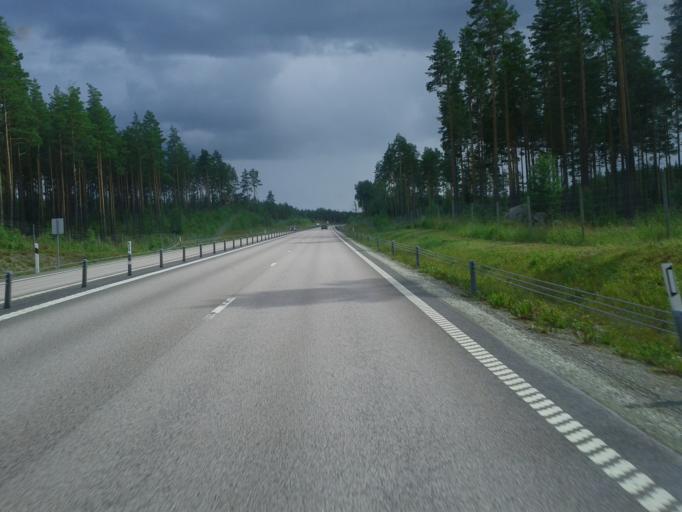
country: SE
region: Vaestmanland
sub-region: Sala Kommun
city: Sala
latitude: 59.9334
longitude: 16.5187
